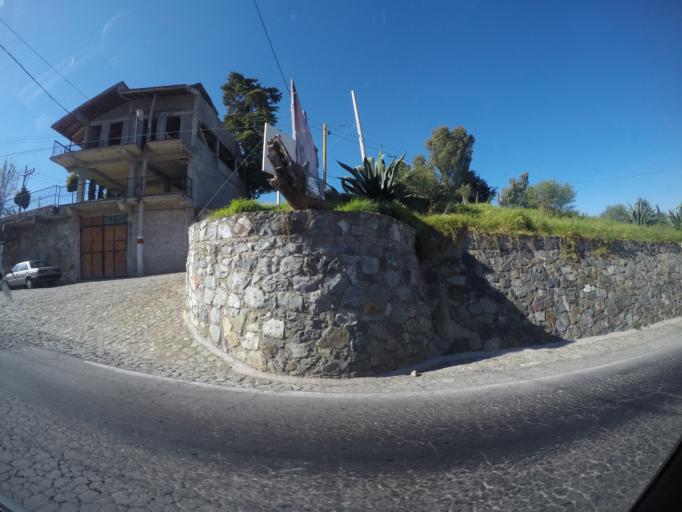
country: MX
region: Hidalgo
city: Mineral del Monte
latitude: 20.1391
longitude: -98.6835
